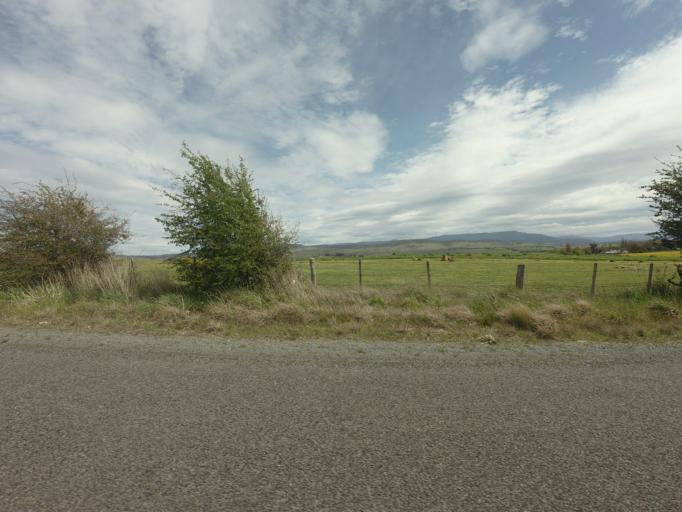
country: AU
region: Tasmania
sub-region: Northern Midlands
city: Evandale
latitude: -41.8819
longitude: 147.3636
